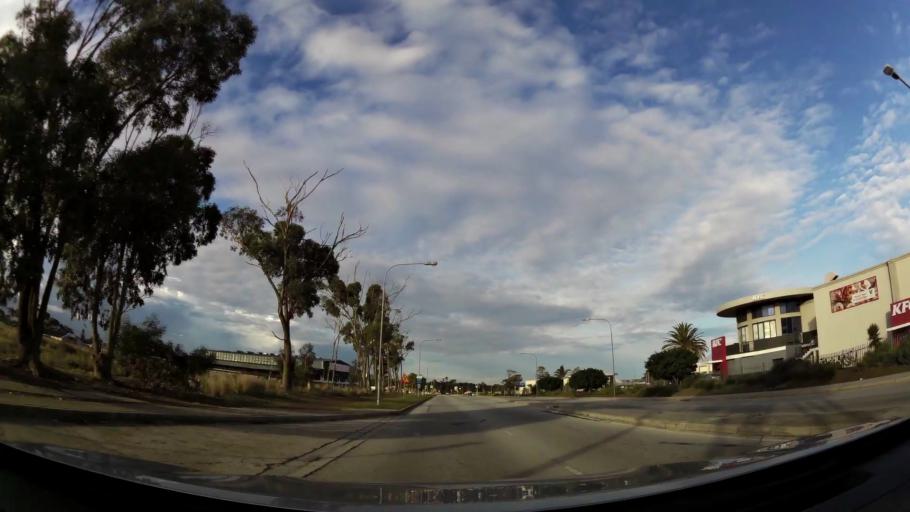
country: ZA
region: Eastern Cape
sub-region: Nelson Mandela Bay Metropolitan Municipality
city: Port Elizabeth
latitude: -33.9573
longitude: 25.5018
